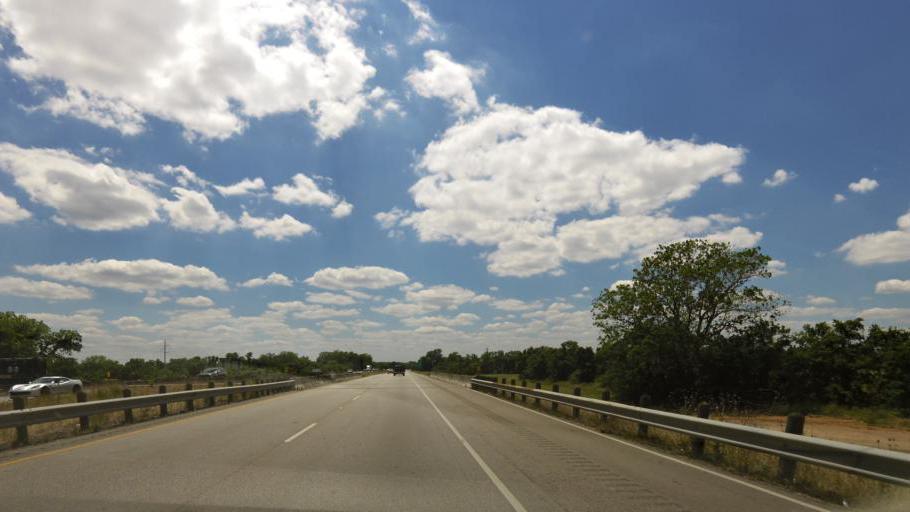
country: US
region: Texas
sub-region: Colorado County
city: Columbus
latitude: 29.7019
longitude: -96.5210
